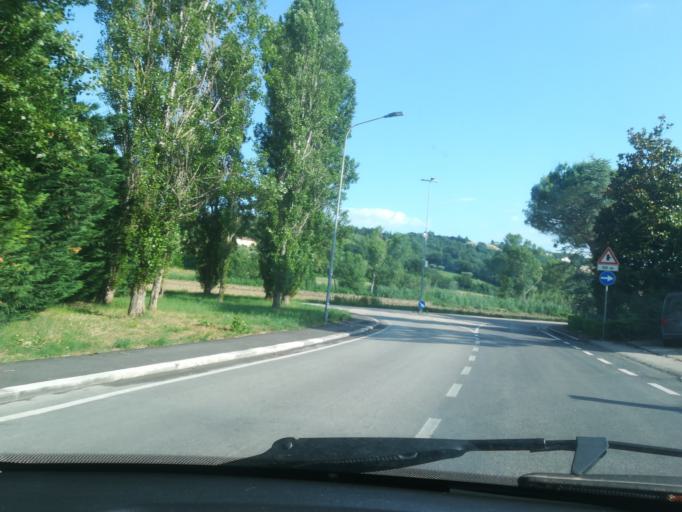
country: IT
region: The Marches
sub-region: Provincia di Macerata
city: Villa Potenza
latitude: 43.3173
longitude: 13.4214
